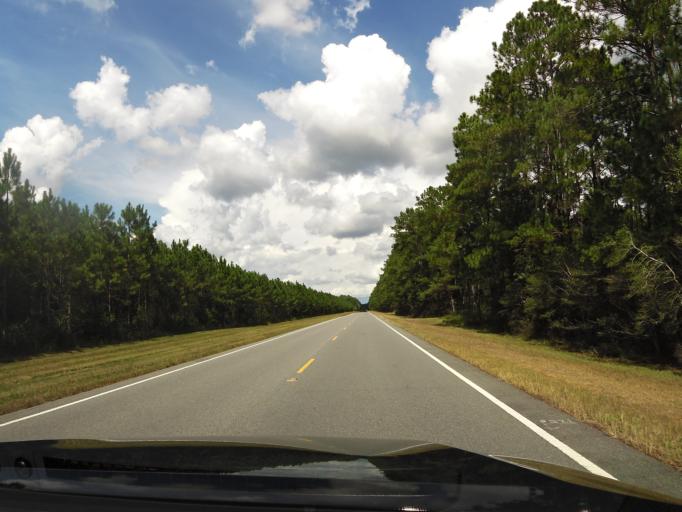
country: US
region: Georgia
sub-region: Charlton County
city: Folkston
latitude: 30.9923
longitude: -82.0262
